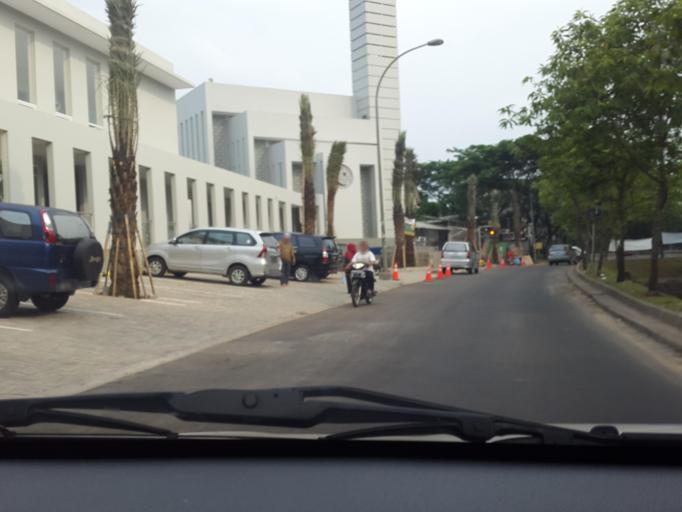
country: ID
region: Banten
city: South Tangerang
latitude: -6.2773
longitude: 106.7001
